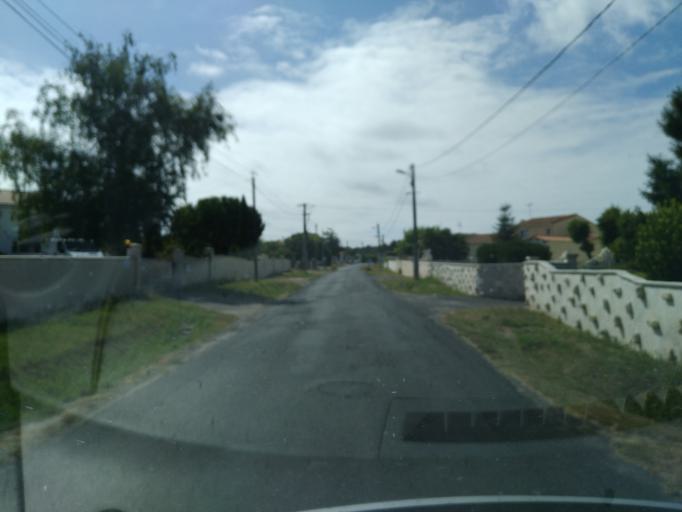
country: FR
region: Poitou-Charentes
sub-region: Departement de la Charente-Maritime
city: Saint-Palais-sur-Mer
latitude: 45.6748
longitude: -1.0874
